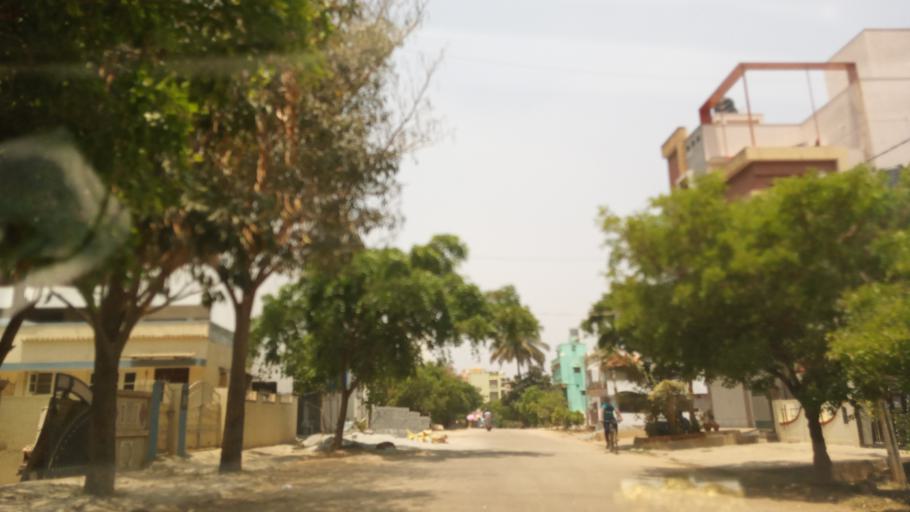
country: IN
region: Karnataka
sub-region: Bangalore Urban
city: Yelahanka
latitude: 13.0400
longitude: 77.5017
